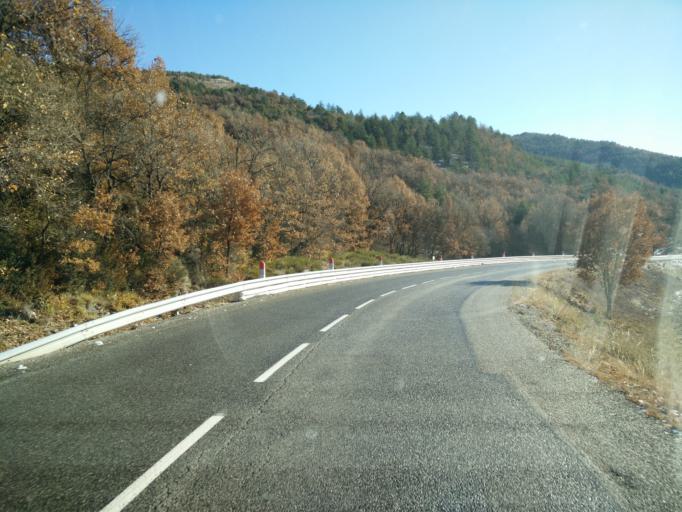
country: FR
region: Provence-Alpes-Cote d'Azur
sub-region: Departement des Alpes-de-Haute-Provence
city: Castellane
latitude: 43.8669
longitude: 6.5077
